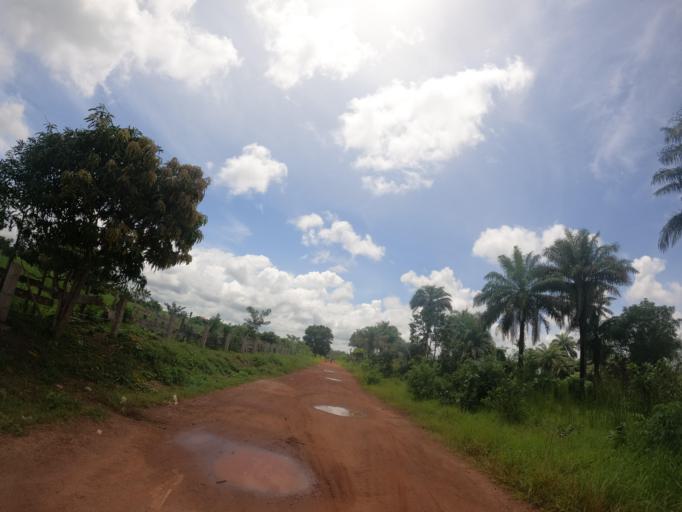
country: SL
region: Northern Province
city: Makeni
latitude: 9.1336
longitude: -12.2401
